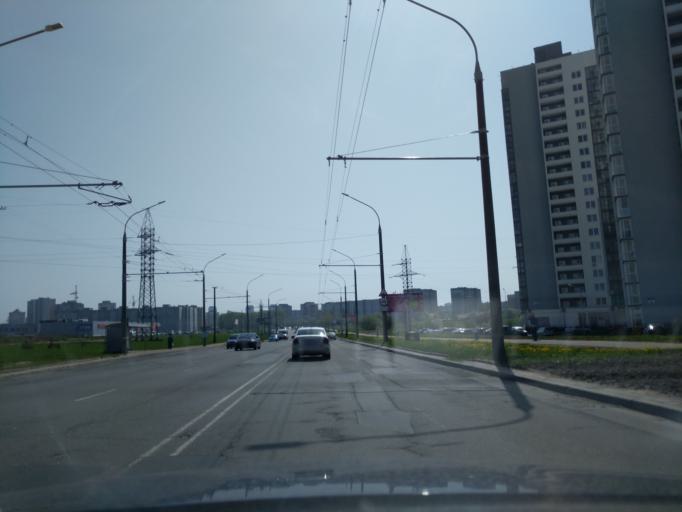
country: BY
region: Minsk
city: Novoye Medvezhino
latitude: 53.8774
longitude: 27.4603
